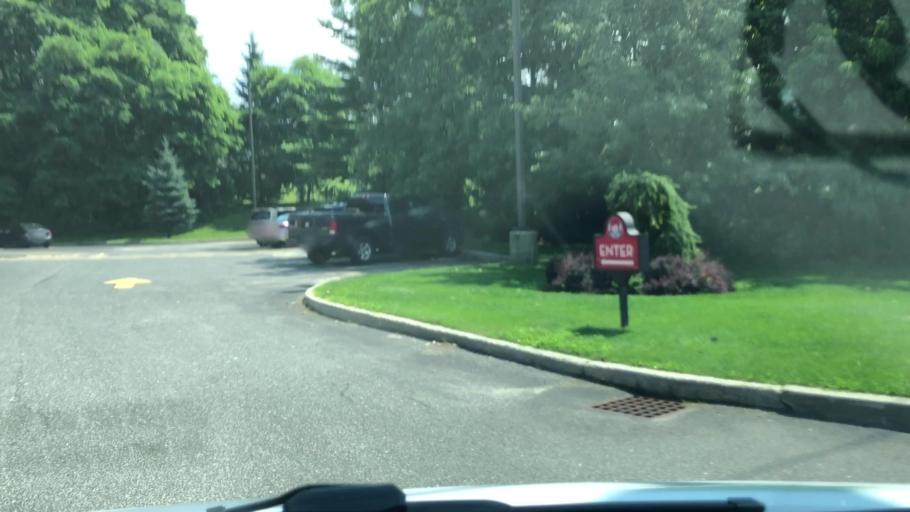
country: US
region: Massachusetts
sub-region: Berkshire County
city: Dalton
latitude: 42.4684
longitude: -73.1961
